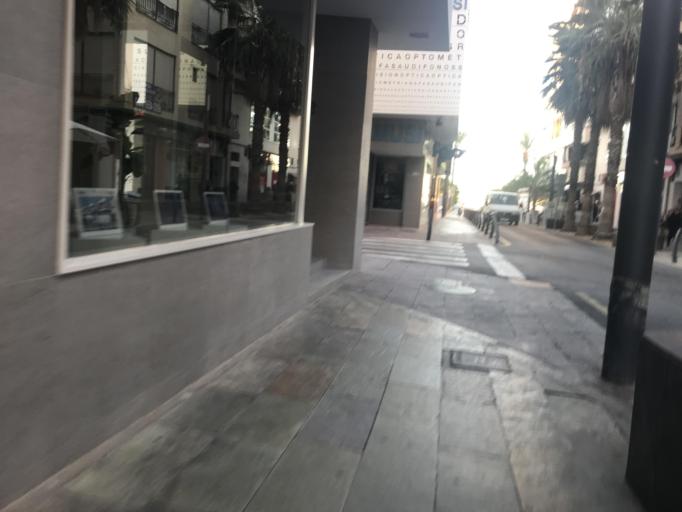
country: ES
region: Valencia
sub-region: Provincia de Alicante
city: Torrevieja
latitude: 37.9764
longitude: -0.6812
